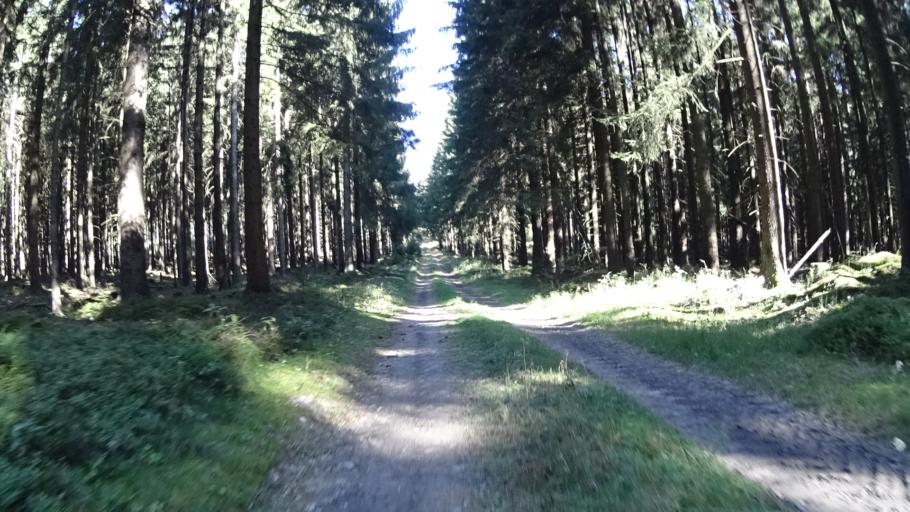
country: DE
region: Thuringia
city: Neustadt am Rennsteig
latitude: 50.6319
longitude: 10.9407
